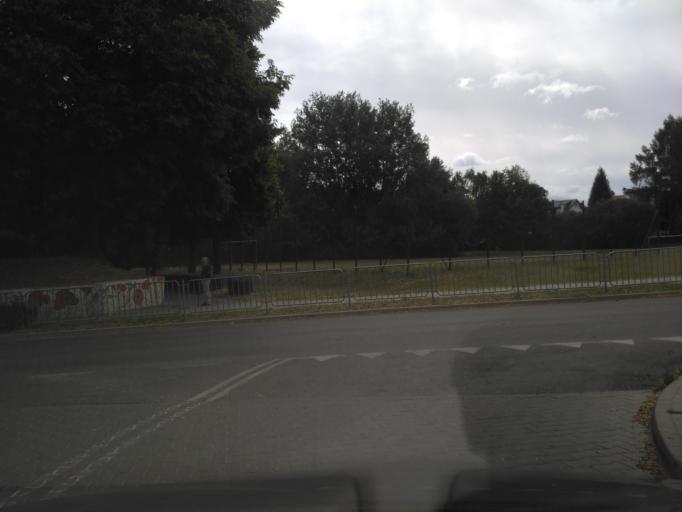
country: PL
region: Lublin Voivodeship
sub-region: Powiat lubelski
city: Lublin
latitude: 51.2278
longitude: 22.5346
